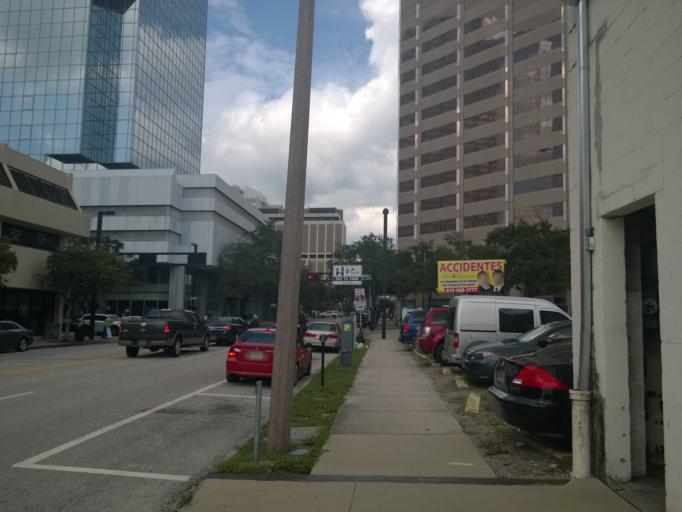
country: US
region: Florida
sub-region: Hillsborough County
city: Tampa
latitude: 27.9475
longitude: -82.4548
